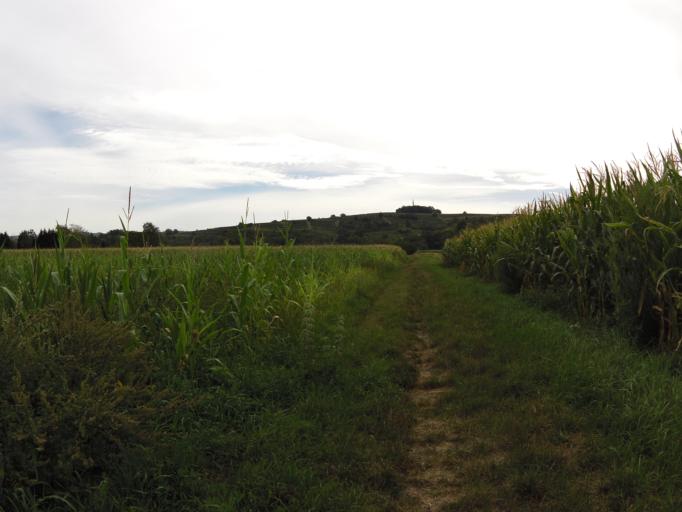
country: DE
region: Baden-Wuerttemberg
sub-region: Freiburg Region
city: Lahr
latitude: 48.3557
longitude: 7.8389
